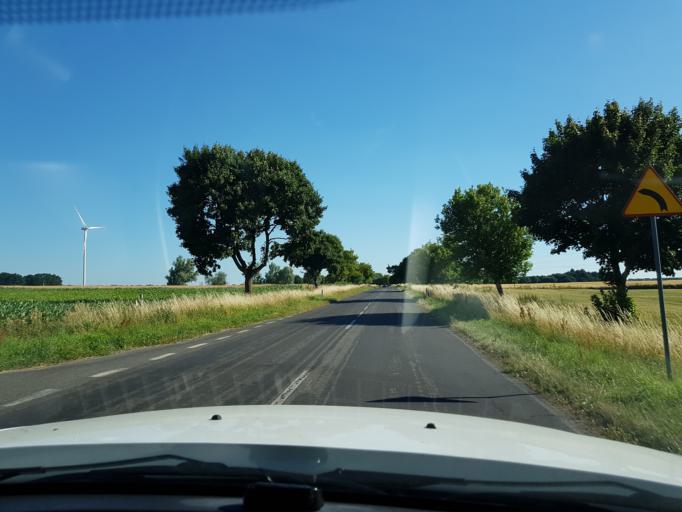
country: PL
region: West Pomeranian Voivodeship
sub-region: Powiat lobeski
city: Lobez
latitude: 53.6791
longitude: 15.6049
